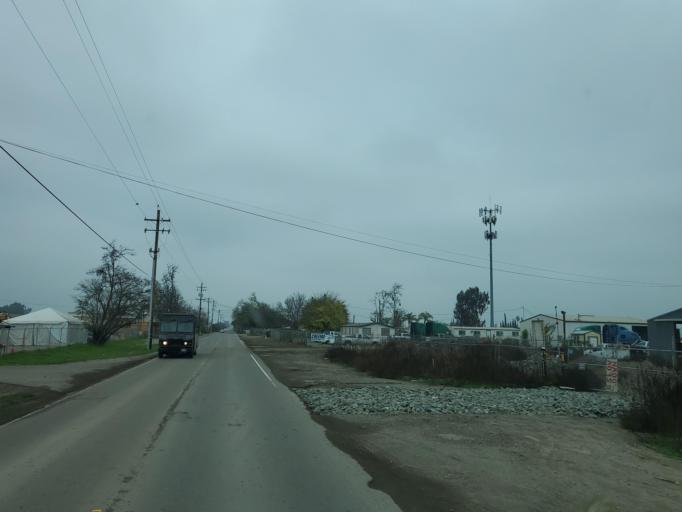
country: US
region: California
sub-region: San Joaquin County
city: Lathrop
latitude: 37.8137
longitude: -121.2715
